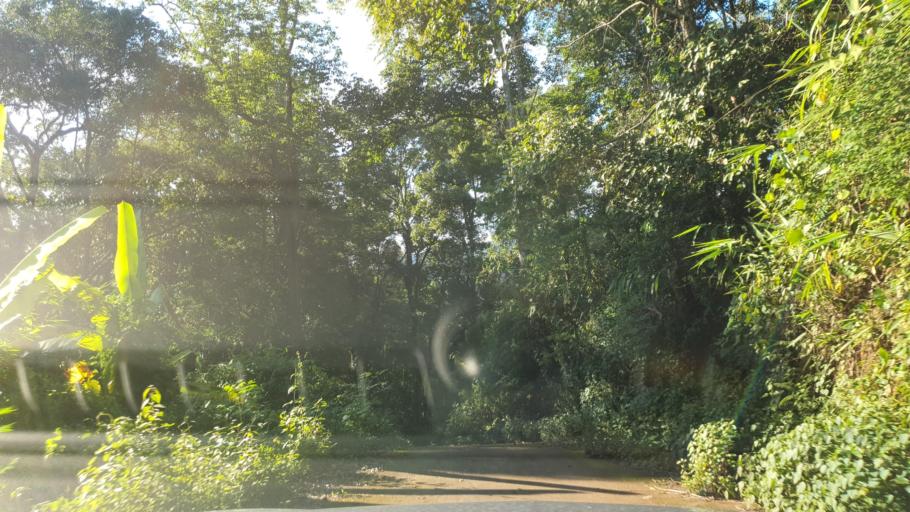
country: TH
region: Chiang Mai
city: Mae On
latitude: 18.8127
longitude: 99.3547
